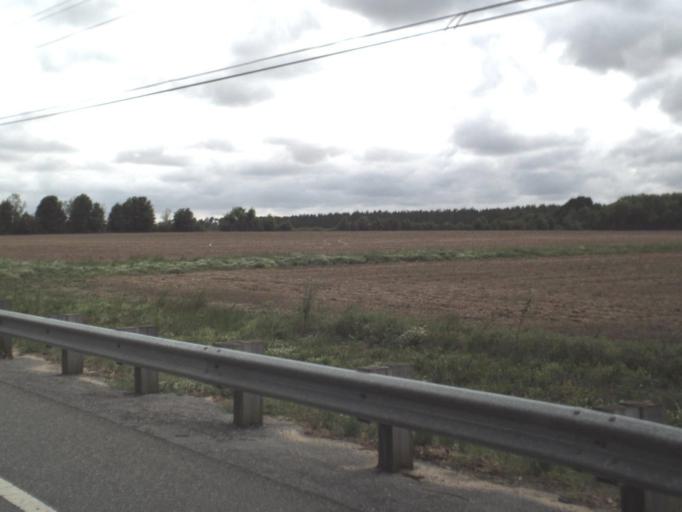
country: US
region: Florida
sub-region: Santa Rosa County
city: Point Baker
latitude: 30.8625
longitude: -87.0527
